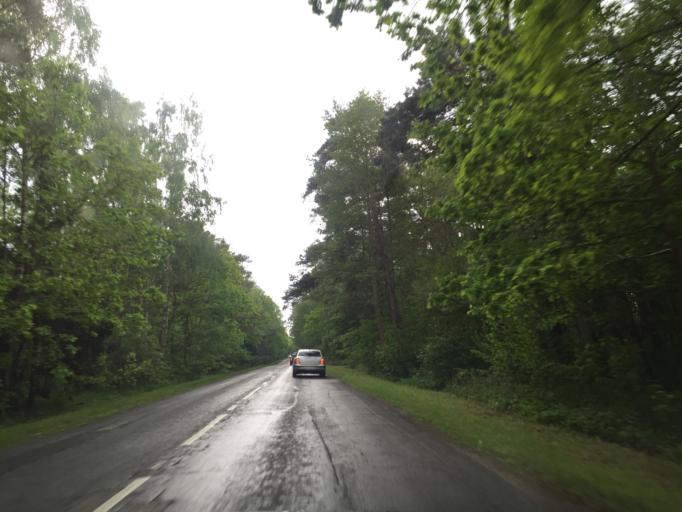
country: LT
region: Klaipedos apskritis
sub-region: Klaipeda
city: Klaipeda
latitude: 55.7419
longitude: 21.0949
